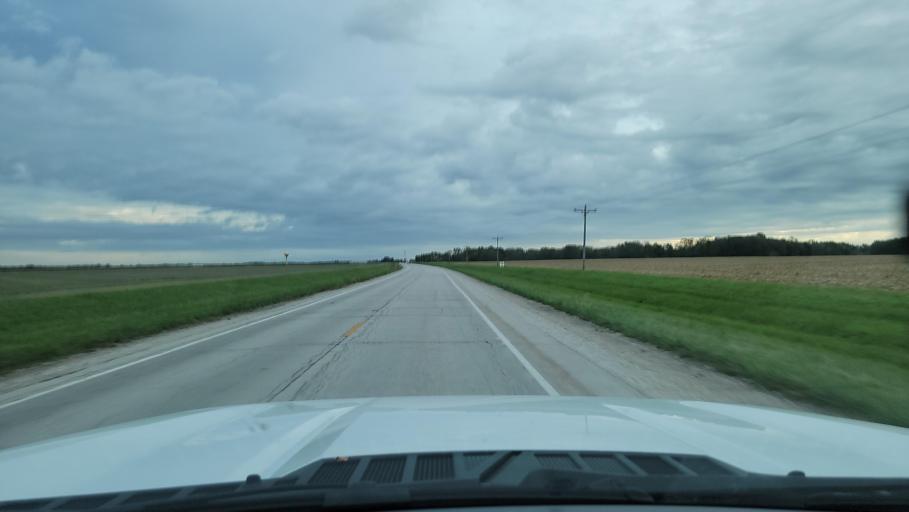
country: US
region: Illinois
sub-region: Schuyler County
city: Rushville
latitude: 40.1030
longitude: -90.5955
